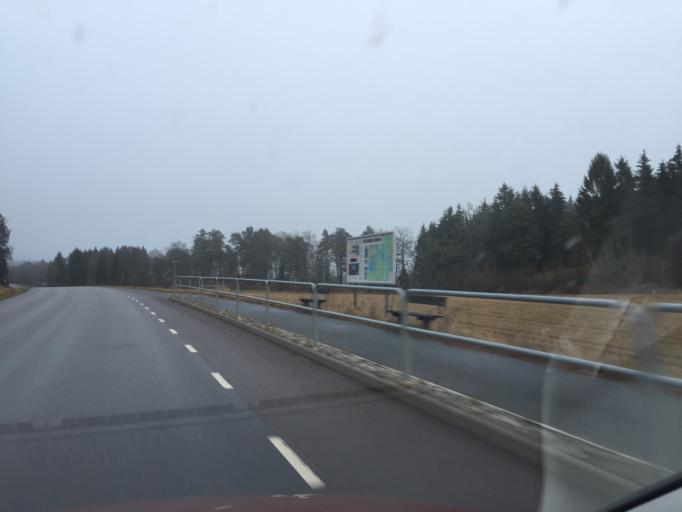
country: SE
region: Stockholm
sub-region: Nynashamns Kommun
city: Osmo
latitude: 59.0262
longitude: 17.9841
